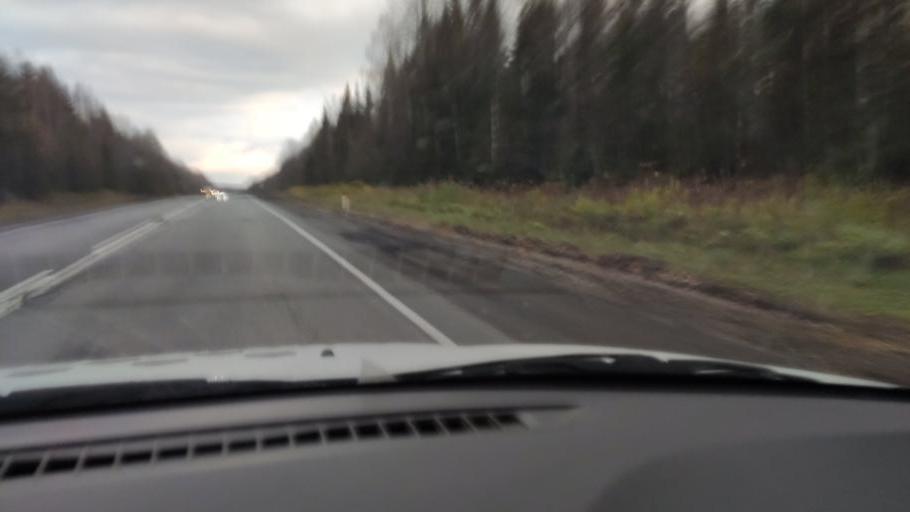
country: RU
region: Kirov
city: Omutninsk
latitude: 58.7585
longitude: 52.0215
